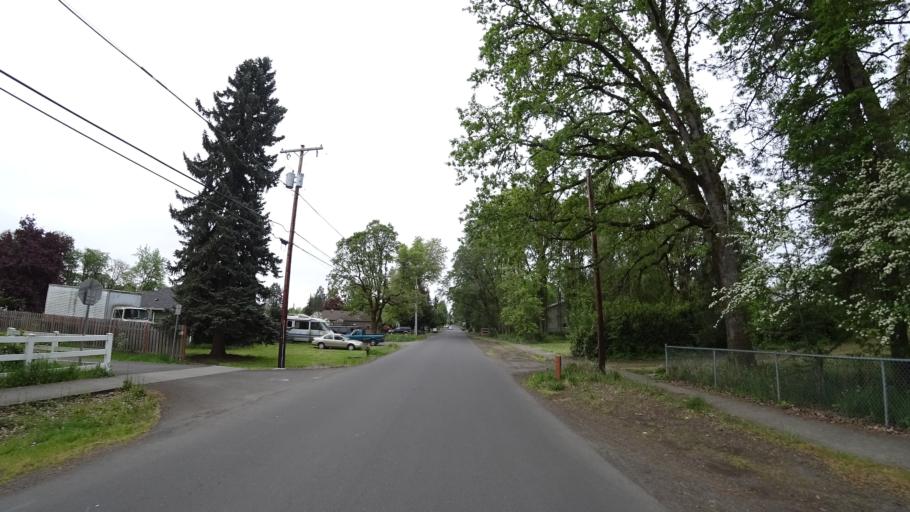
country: US
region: Oregon
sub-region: Washington County
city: Aloha
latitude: 45.5046
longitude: -122.8701
